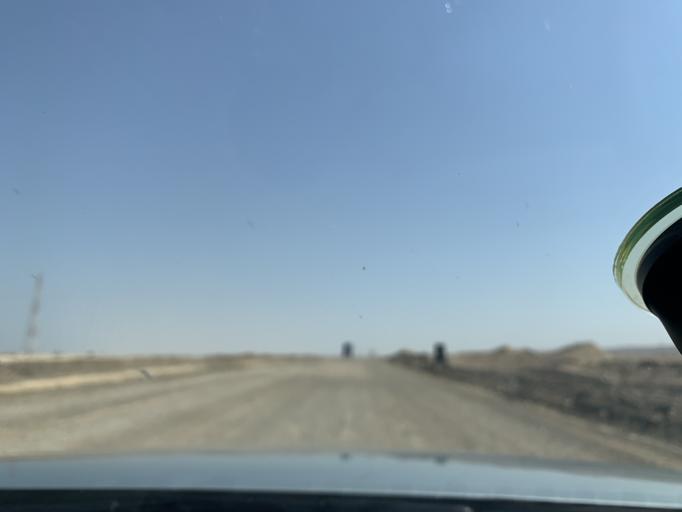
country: EG
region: As Suways
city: Ain Sukhna
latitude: 28.9688
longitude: 32.6186
